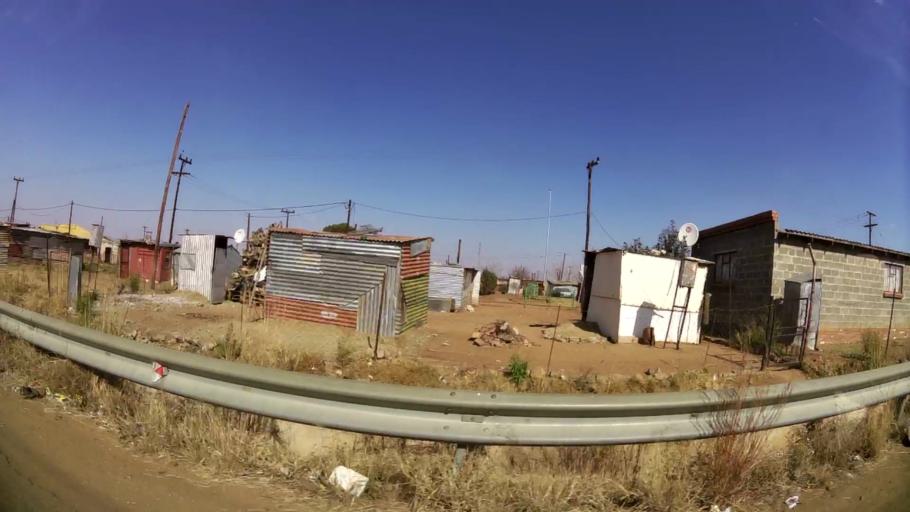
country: ZA
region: Orange Free State
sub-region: Mangaung Metropolitan Municipality
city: Bloemfontein
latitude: -29.1535
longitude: 26.3003
